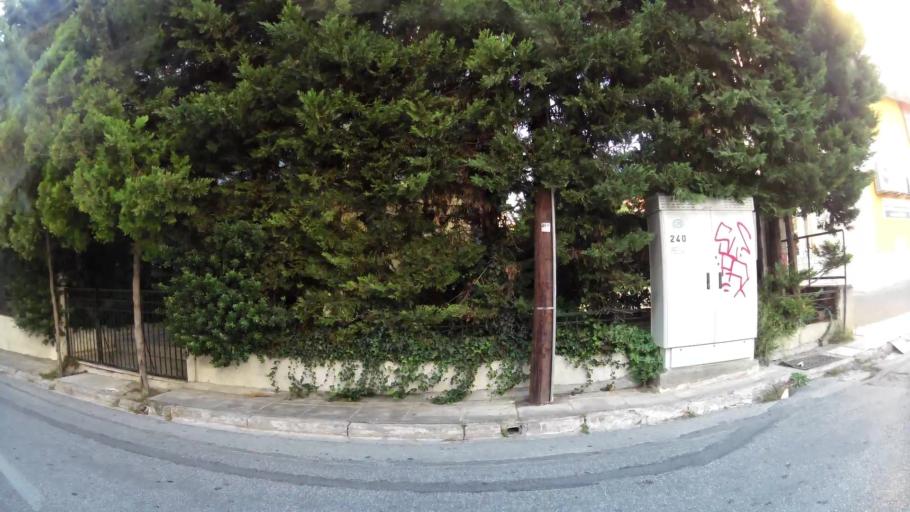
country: GR
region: Attica
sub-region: Nomarchia Anatolikis Attikis
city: Pallini
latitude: 38.0033
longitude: 23.8846
